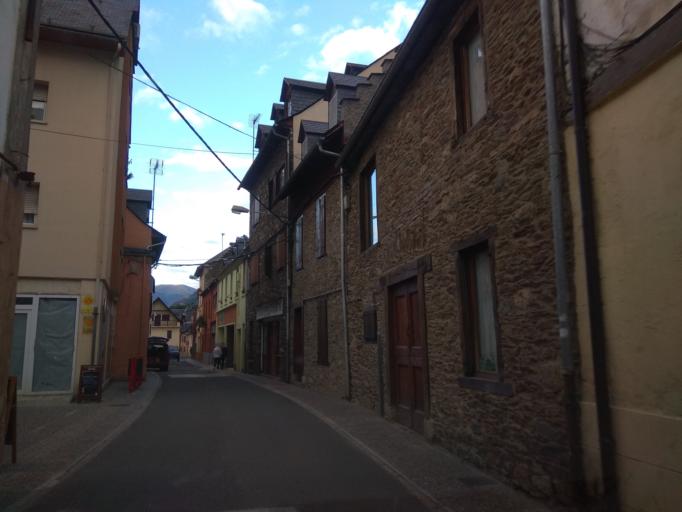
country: ES
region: Catalonia
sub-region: Provincia de Lleida
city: Les
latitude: 42.8104
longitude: 0.7114
